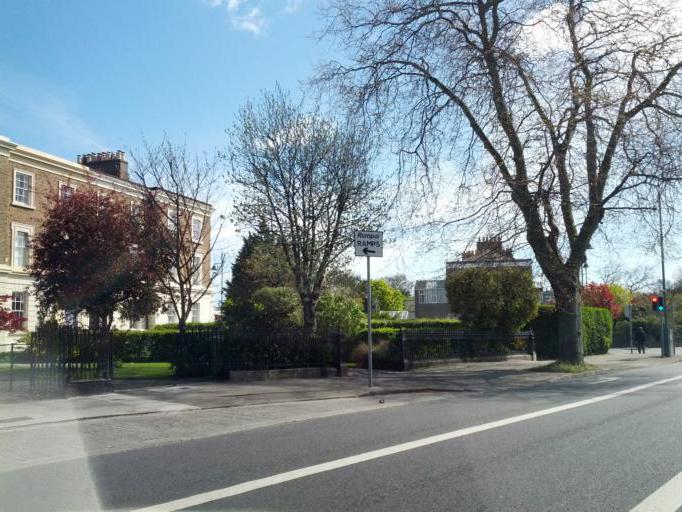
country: IE
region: Leinster
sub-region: Dublin City
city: Dublin
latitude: 53.3284
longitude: -6.2464
